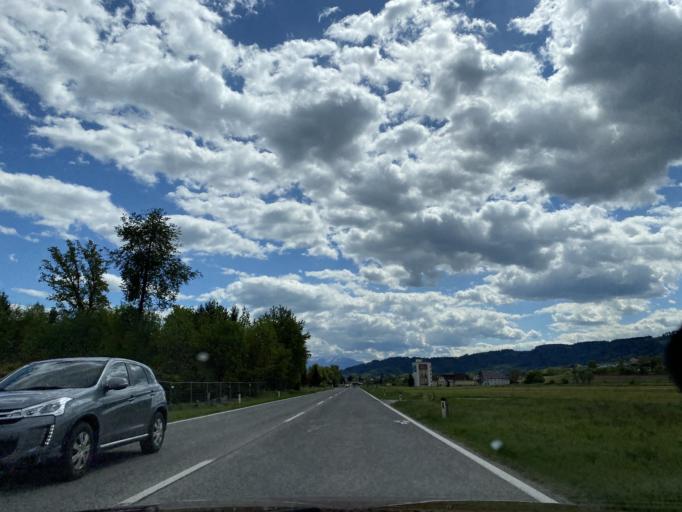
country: AT
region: Carinthia
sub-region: Politischer Bezirk Wolfsberg
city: Sankt Andrae
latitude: 46.8016
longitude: 14.8288
